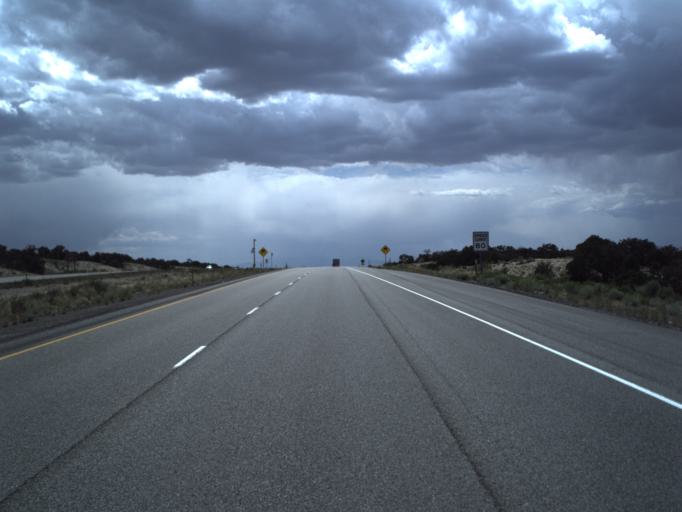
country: US
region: Utah
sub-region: Emery County
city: Ferron
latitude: 38.8530
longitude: -110.9248
